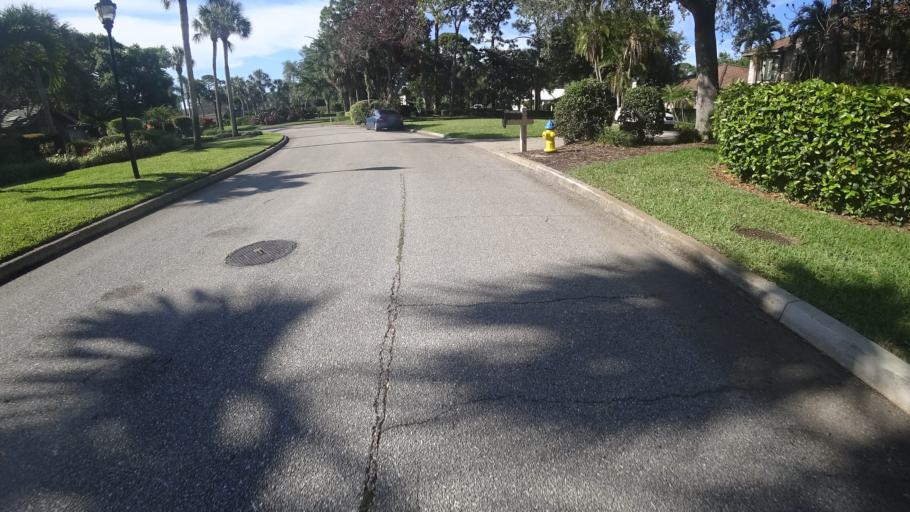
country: US
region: Florida
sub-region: Manatee County
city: West Bradenton
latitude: 27.5194
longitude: -82.6470
